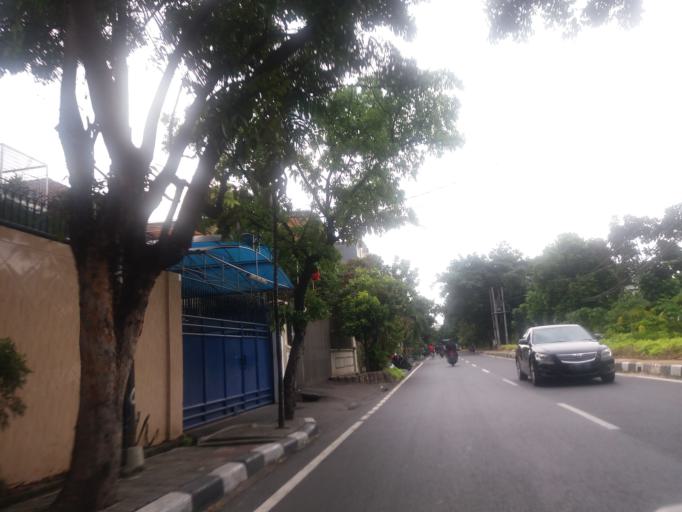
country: ID
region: Jakarta Raya
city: Jakarta
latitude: -6.1538
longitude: 106.8355
